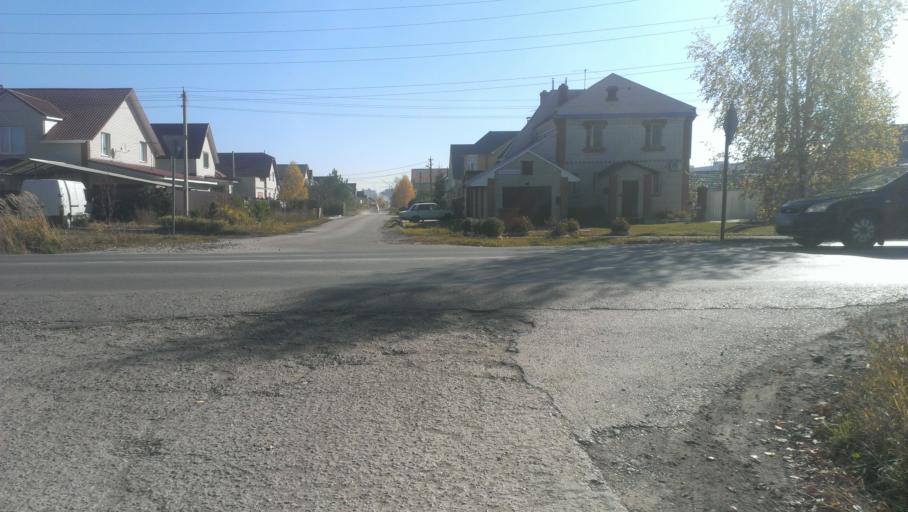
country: RU
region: Altai Krai
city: Novosilikatnyy
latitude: 53.3536
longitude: 83.6333
